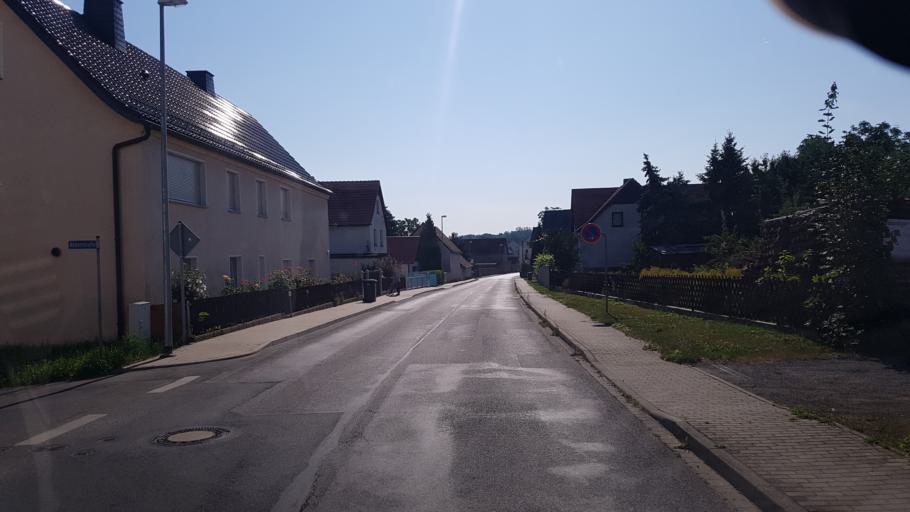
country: DE
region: Brandenburg
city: Hirschfeld
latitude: 51.3881
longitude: 13.6141
